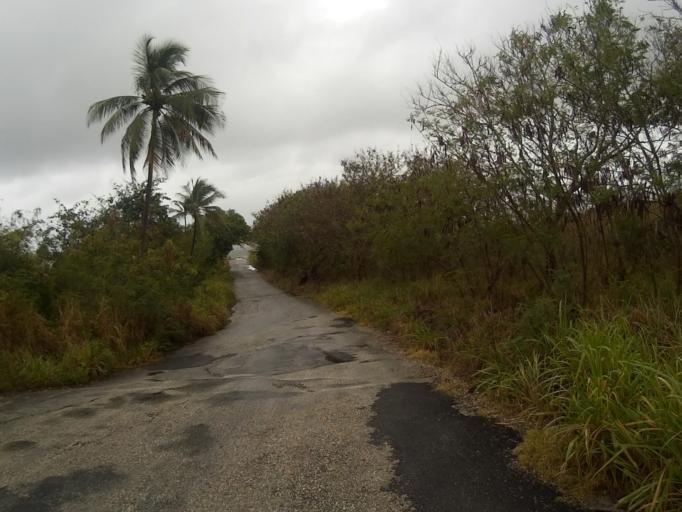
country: BB
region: Saint Andrew
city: Greenland
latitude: 13.2731
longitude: -59.5783
